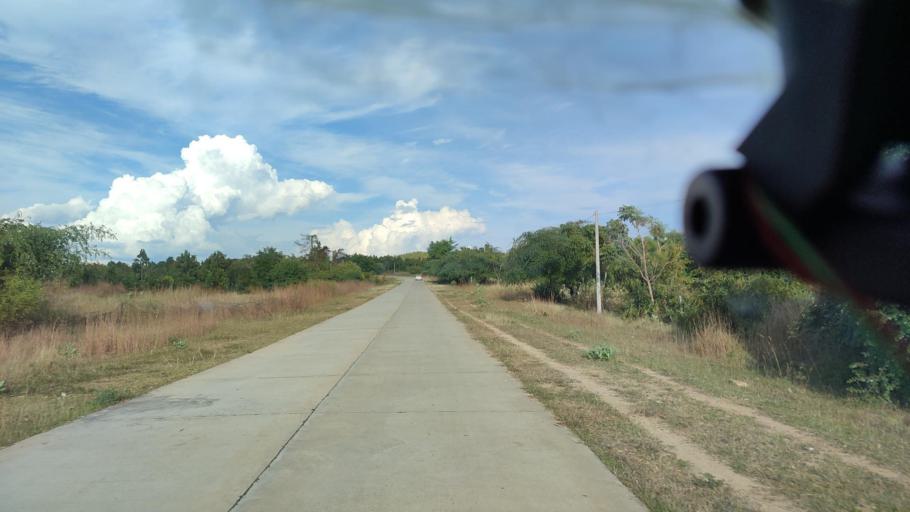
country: MM
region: Mandalay
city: Yamethin
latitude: 20.1048
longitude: 96.0390
